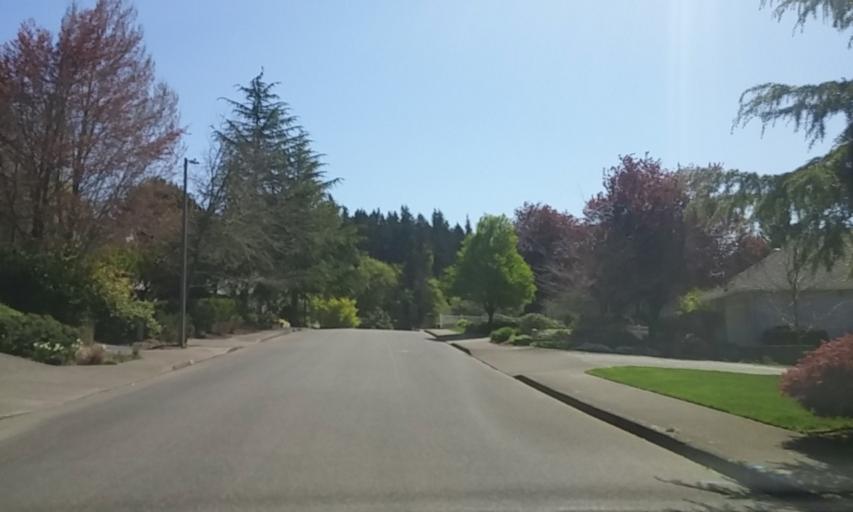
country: US
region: Oregon
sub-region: Washington County
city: West Haven
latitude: 45.5250
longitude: -122.7639
